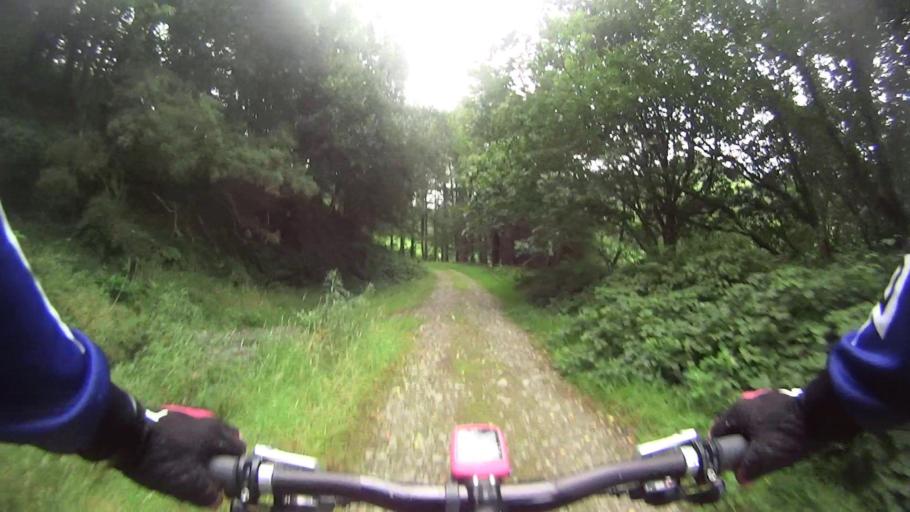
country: GB
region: Wales
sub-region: County of Ceredigion
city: Bow Street
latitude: 52.4177
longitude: -3.9102
